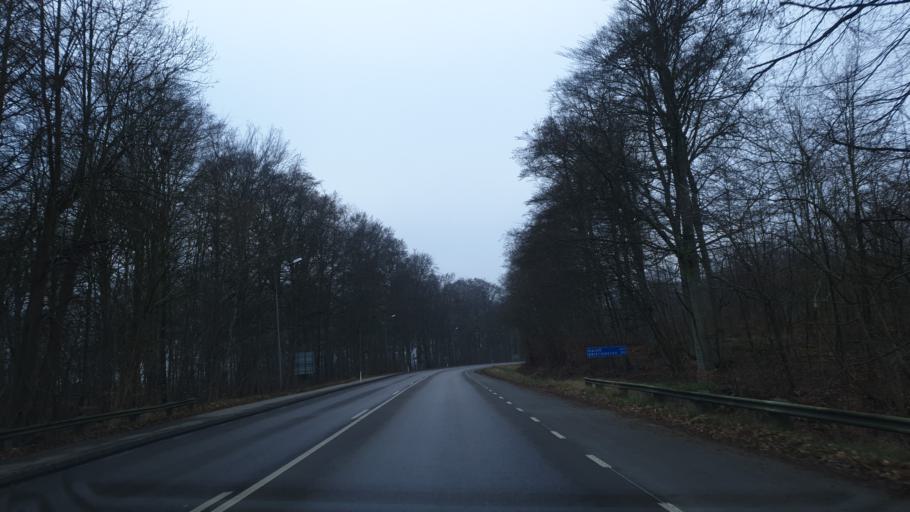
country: SE
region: Blekinge
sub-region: Solvesborgs Kommun
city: Soelvesborg
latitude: 56.0579
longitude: 14.5567
